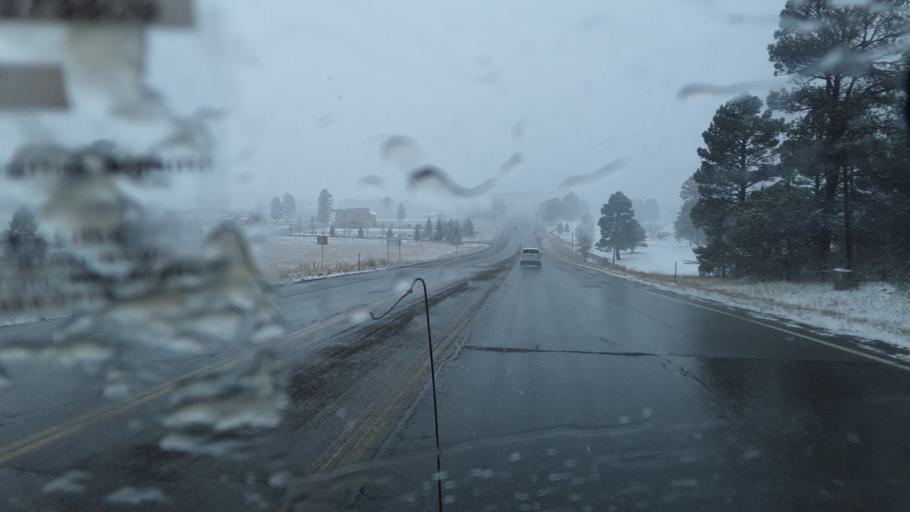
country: US
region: Colorado
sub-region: Archuleta County
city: Pagosa Springs
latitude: 37.2665
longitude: -107.0553
